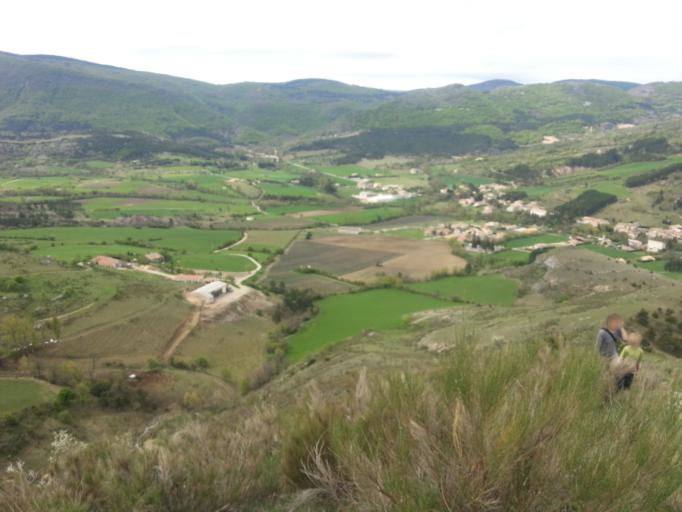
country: FR
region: Provence-Alpes-Cote d'Azur
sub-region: Departement du Vaucluse
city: Sault
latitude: 44.2084
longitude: 5.5476
